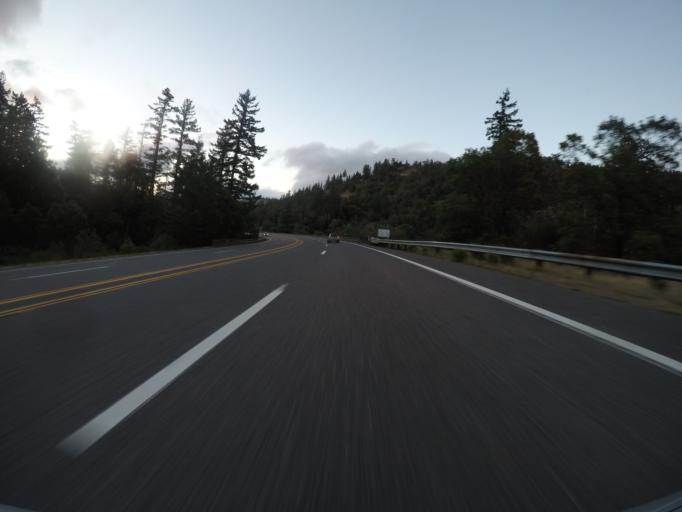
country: US
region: California
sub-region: Humboldt County
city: Redway
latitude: 40.0613
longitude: -123.7834
